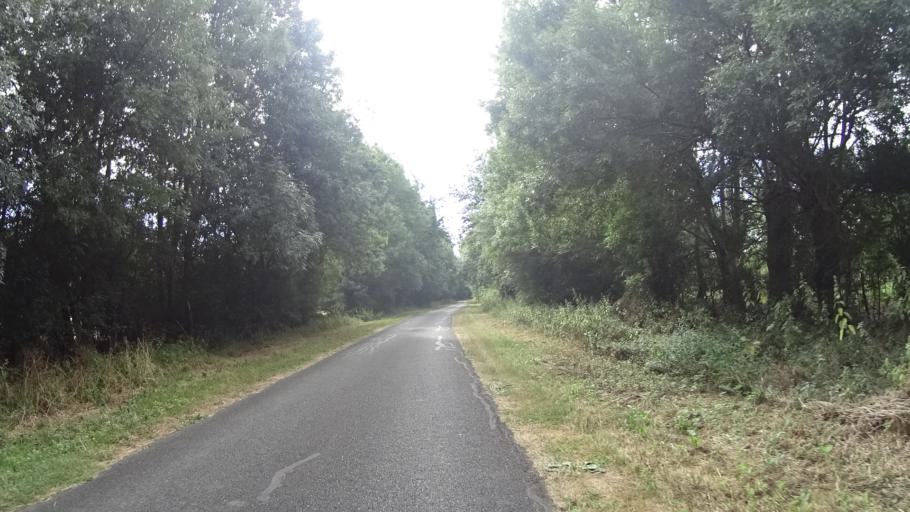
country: FR
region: Centre
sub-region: Departement d'Indre-et-Loire
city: Chouze-sur-Loire
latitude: 47.2054
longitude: 0.0973
